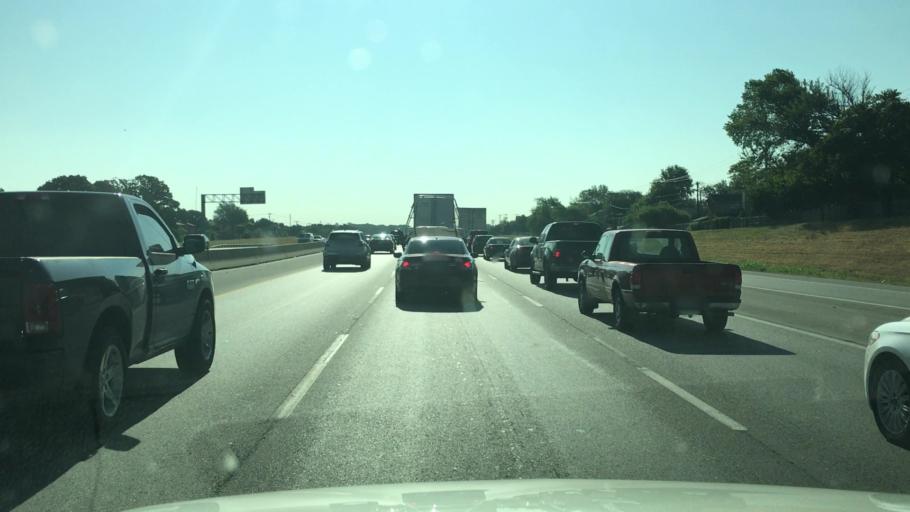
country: US
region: Texas
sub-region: Tarrant County
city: Pantego
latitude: 32.7599
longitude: -97.1636
